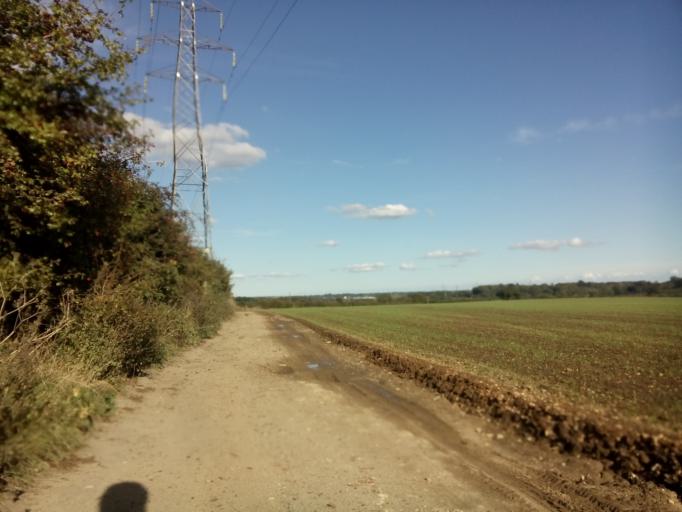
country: GB
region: England
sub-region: Suffolk
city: Ipswich
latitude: 52.0235
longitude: 1.1154
